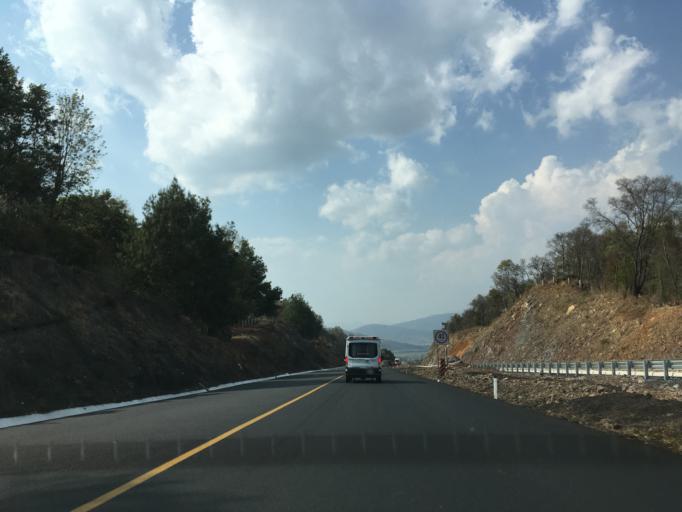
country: MX
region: Michoacan
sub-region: Patzcuaro
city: Colonia Vista Bella (Lomas del Peaje)
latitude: 19.5166
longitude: -101.5734
